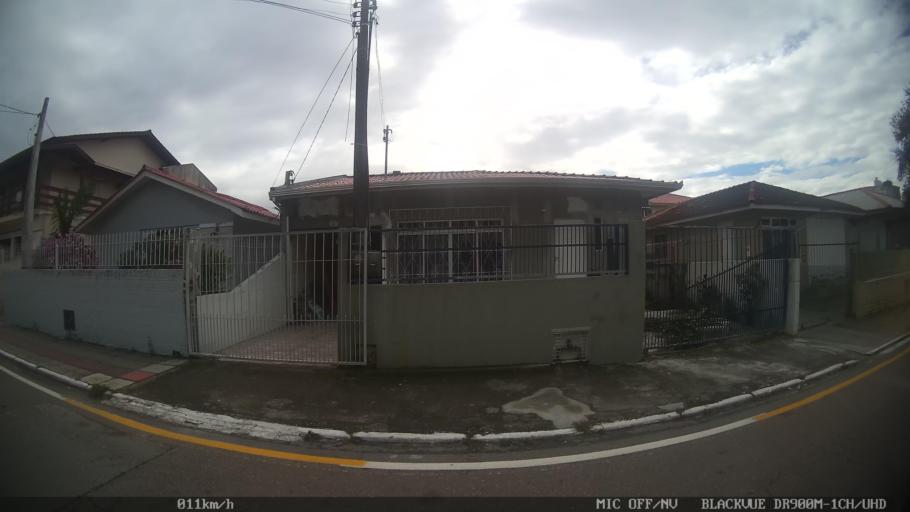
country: BR
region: Santa Catarina
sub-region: Sao Jose
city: Campinas
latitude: -27.5766
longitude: -48.6202
